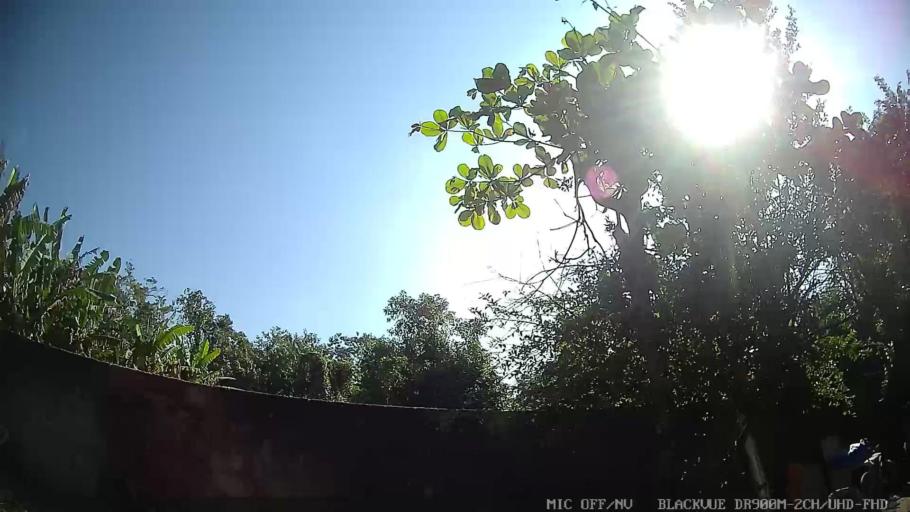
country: BR
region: Sao Paulo
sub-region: Guaruja
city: Guaruja
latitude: -24.0097
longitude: -46.2804
